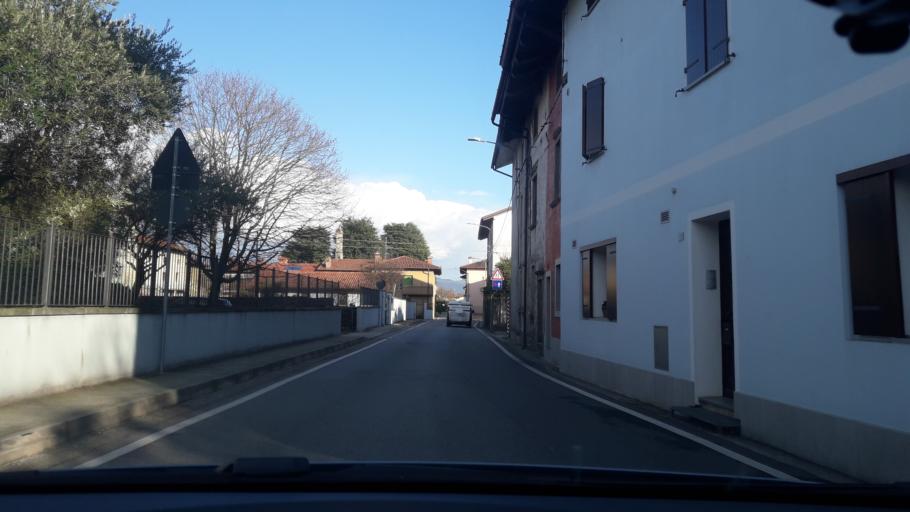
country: IT
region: Friuli Venezia Giulia
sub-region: Provincia di Udine
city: Reana del Roiale
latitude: 46.1443
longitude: 13.2312
